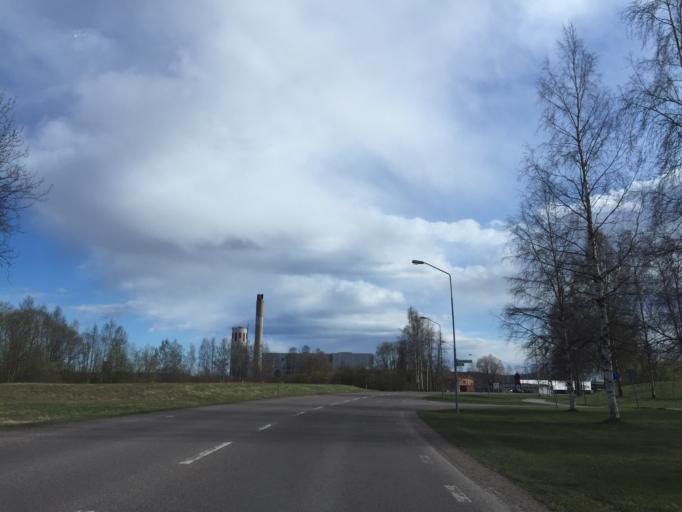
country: SE
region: Dalarna
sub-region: Borlange Kommun
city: Borlaenge
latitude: 60.4814
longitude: 15.4086
